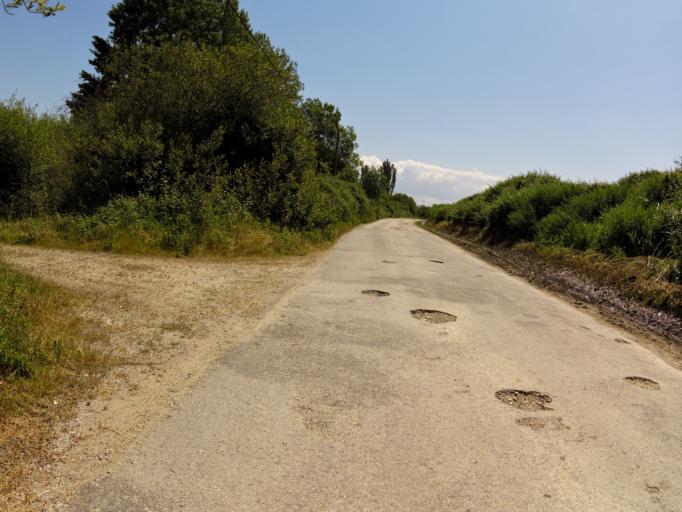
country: PT
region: Coimbra
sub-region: Montemor-O-Velho
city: Montemor-o-Velho
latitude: 40.1489
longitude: -8.7181
